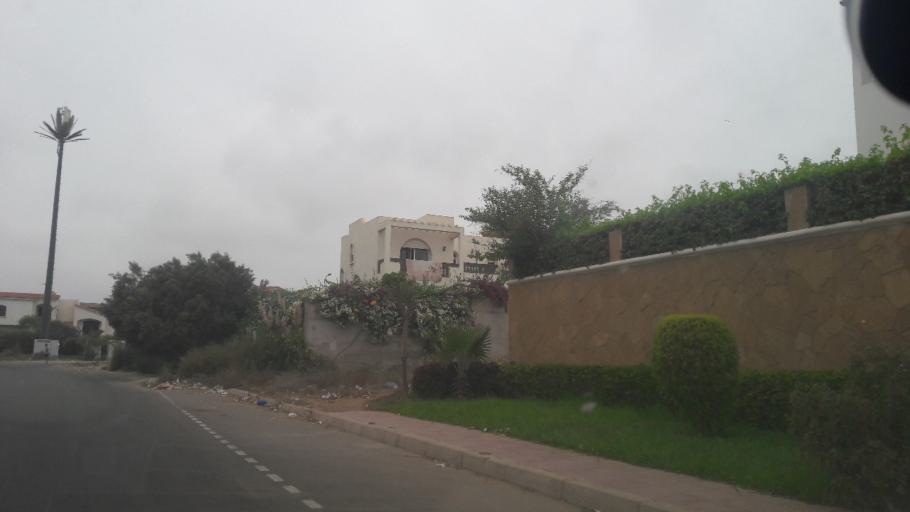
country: MA
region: Souss-Massa-Draa
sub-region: Agadir-Ida-ou-Tnan
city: Agadir
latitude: 30.3891
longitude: -9.5898
